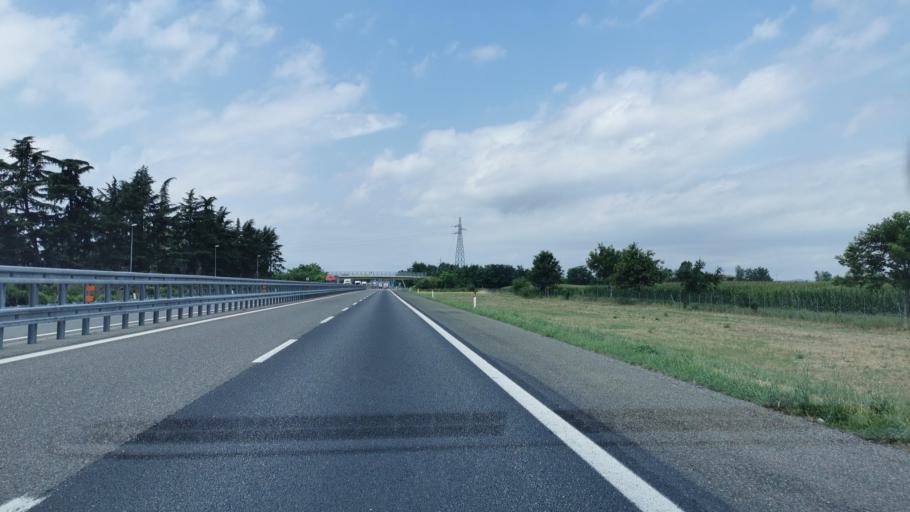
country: IT
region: Piedmont
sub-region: Provincia di Alessandria
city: Valmadonna
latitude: 44.9424
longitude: 8.6086
